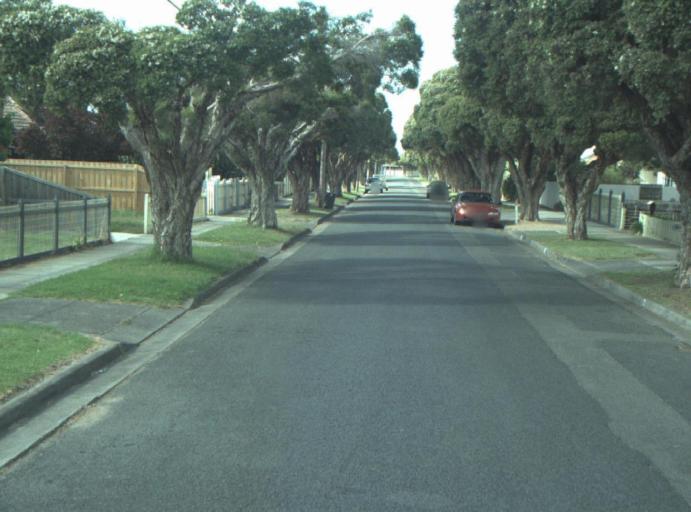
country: AU
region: Victoria
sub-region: Greater Geelong
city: Breakwater
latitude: -38.1759
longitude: 144.3381
